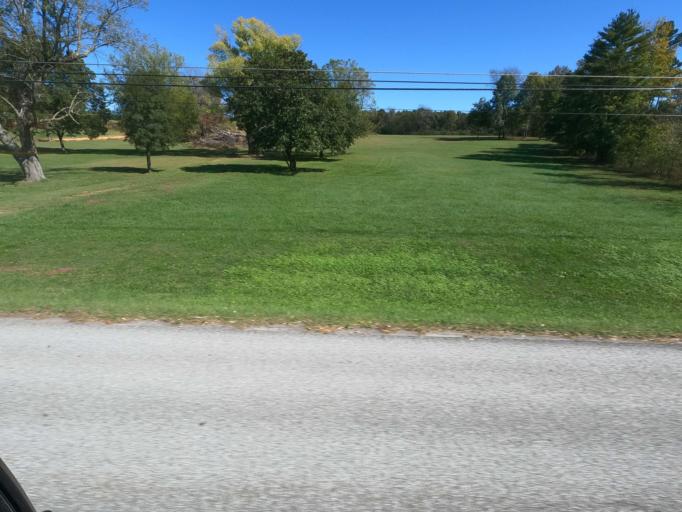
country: US
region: Tennessee
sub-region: Maury County
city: Mount Pleasant
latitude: 35.3946
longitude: -87.2775
